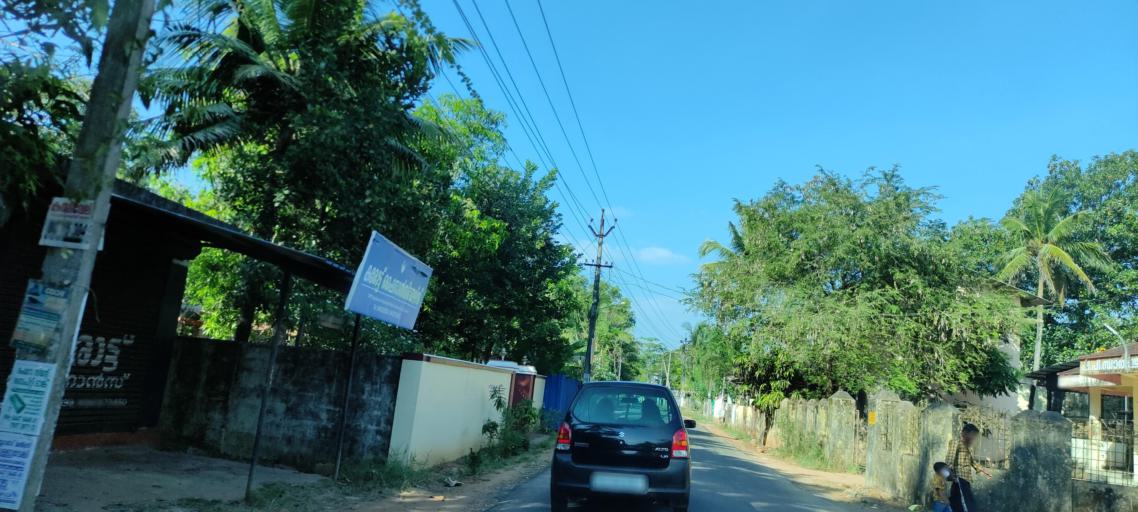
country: IN
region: Kerala
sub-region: Alappuzha
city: Shertallai
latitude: 9.6217
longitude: 76.3424
